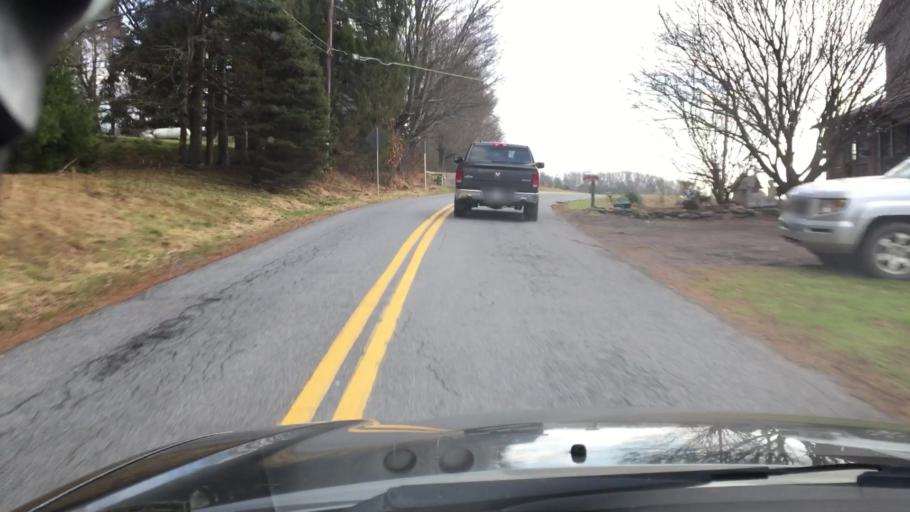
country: US
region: Pennsylvania
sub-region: Luzerne County
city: Back Mountain
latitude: 41.3233
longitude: -76.0666
